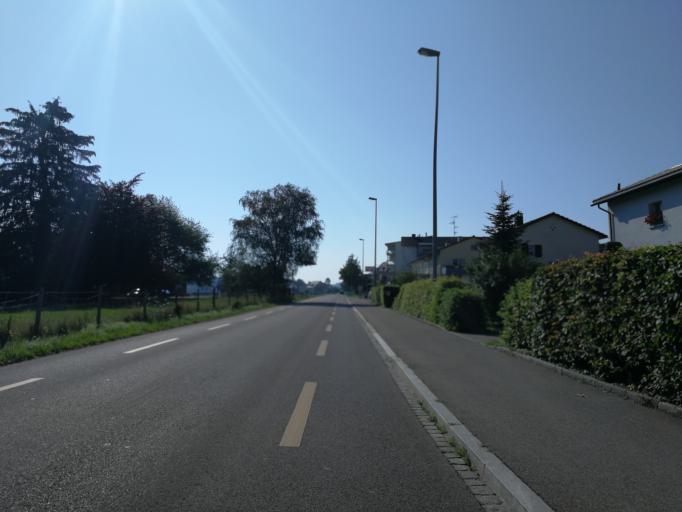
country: CH
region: Thurgau
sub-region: Frauenfeld District
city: Diessenhofen
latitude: 47.6871
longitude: 8.7573
